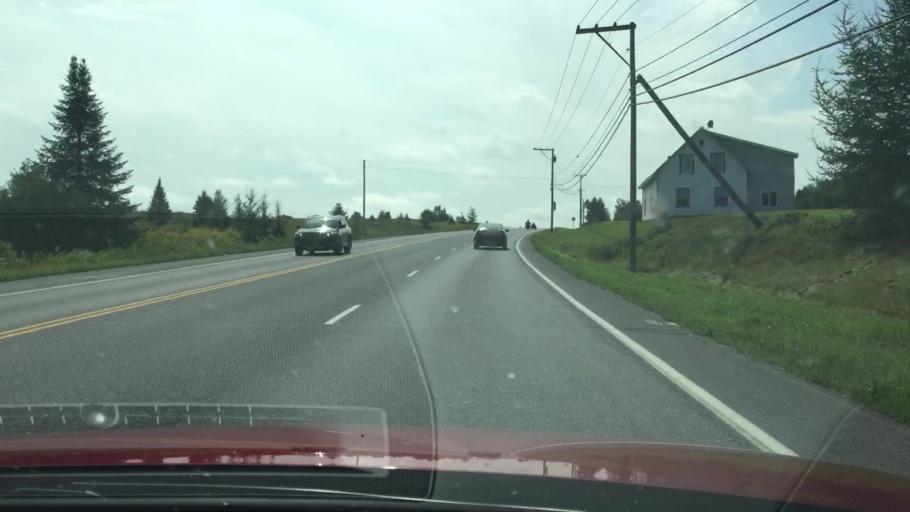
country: CA
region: New Brunswick
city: Florenceville-Bristol
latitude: 46.4158
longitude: -67.8435
